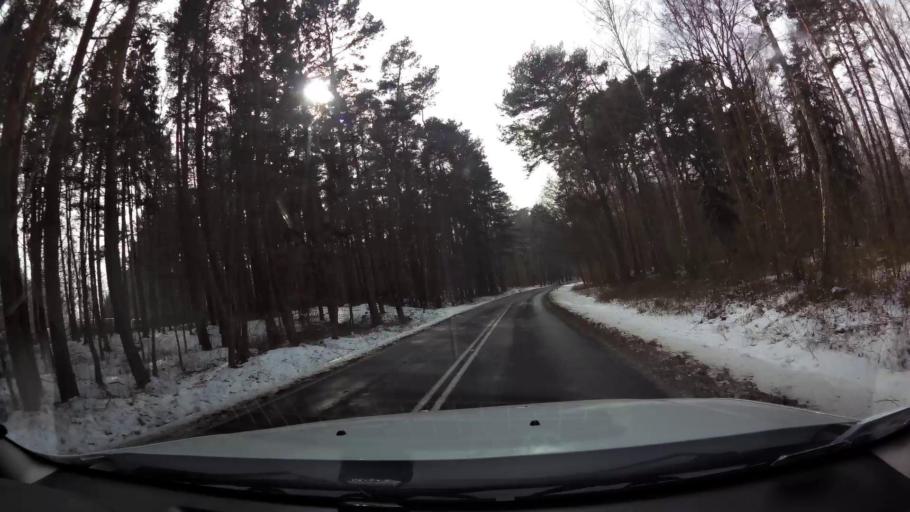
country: PL
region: West Pomeranian Voivodeship
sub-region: Powiat kamienski
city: Dziwnow
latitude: 53.9946
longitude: 14.6464
